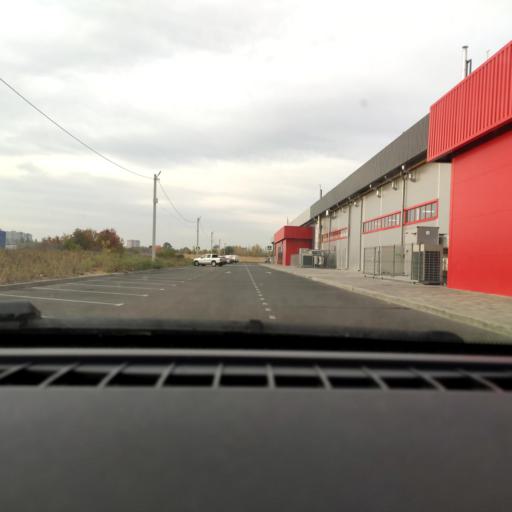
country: RU
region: Voronezj
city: Voronezh
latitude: 51.6797
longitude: 39.2827
